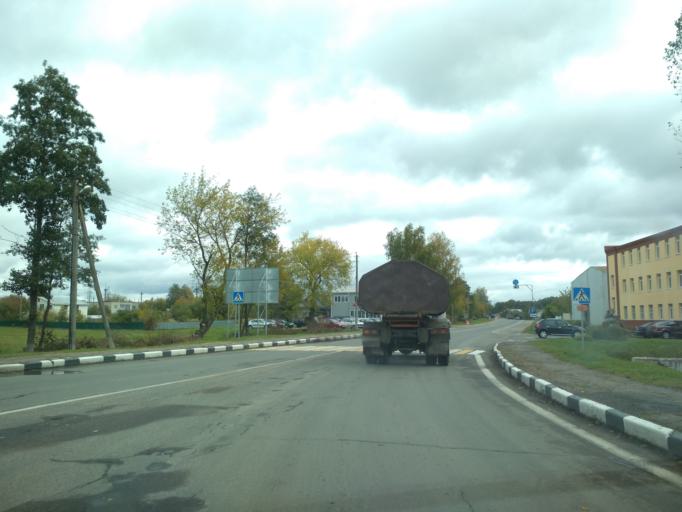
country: BY
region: Minsk
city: Mar''ina Horka
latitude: 53.5249
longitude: 28.1418
